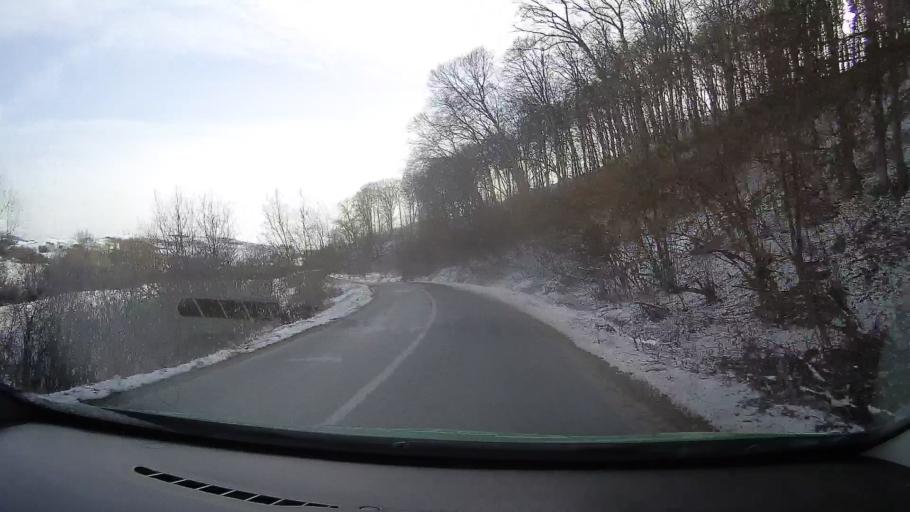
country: RO
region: Mures
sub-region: Comuna Apold
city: Saes
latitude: 46.1718
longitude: 24.7563
